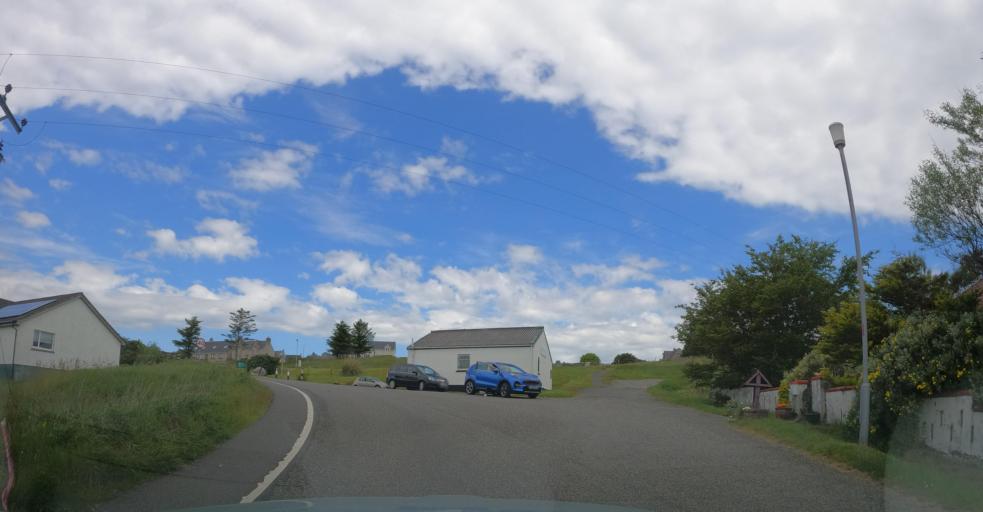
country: GB
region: Scotland
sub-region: Eilean Siar
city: Isle of Lewis
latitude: 58.2760
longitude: -6.2975
